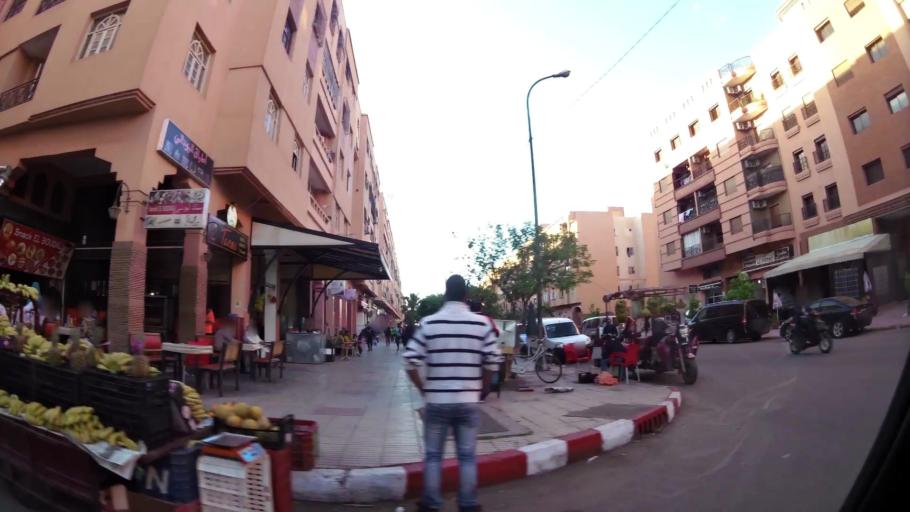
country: MA
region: Marrakech-Tensift-Al Haouz
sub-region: Marrakech
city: Marrakesh
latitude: 31.6213
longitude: -8.0277
